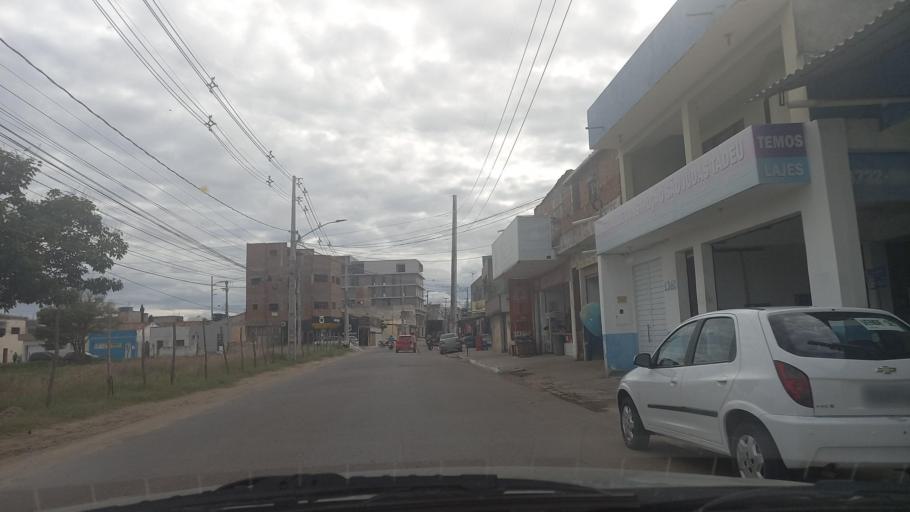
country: BR
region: Pernambuco
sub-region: Caruaru
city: Caruaru
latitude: -8.2866
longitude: -35.9932
